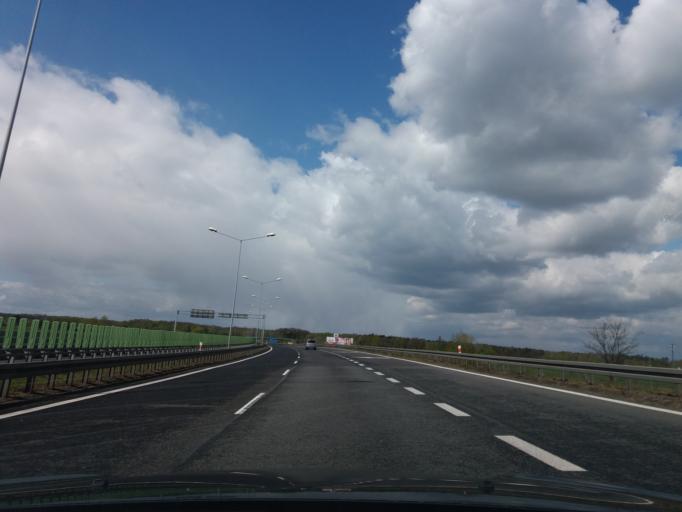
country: PL
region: Silesian Voivodeship
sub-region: Powiat gliwicki
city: Sosnicowice
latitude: 50.3478
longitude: 18.5377
